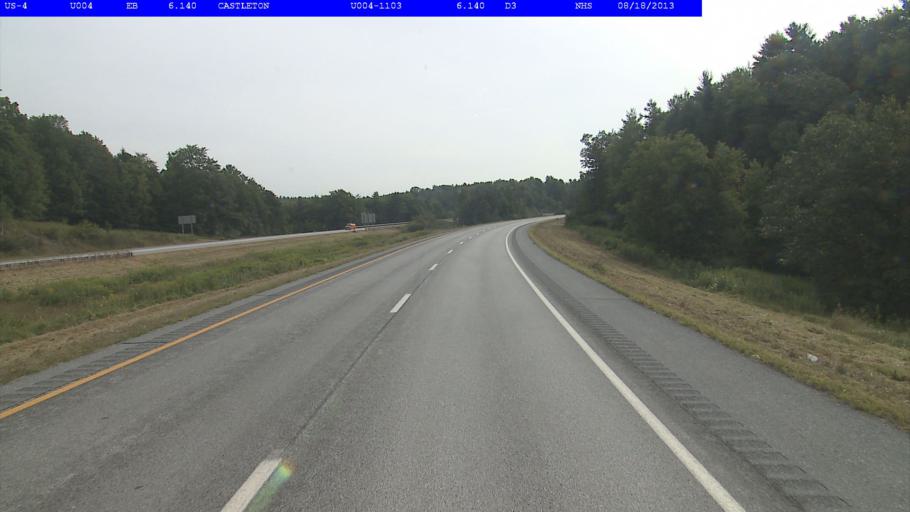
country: US
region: Vermont
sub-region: Rutland County
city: Castleton
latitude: 43.6220
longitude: -73.1957
